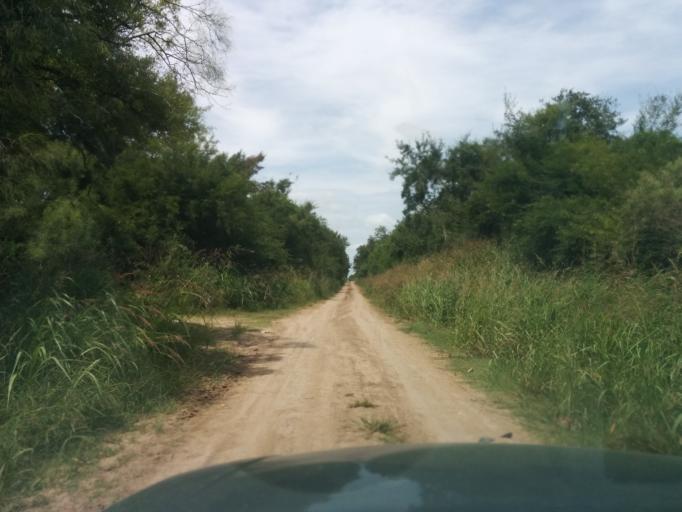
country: AR
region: Buenos Aires
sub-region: Partido de Campana
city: Campana
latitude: -34.2782
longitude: -58.9577
